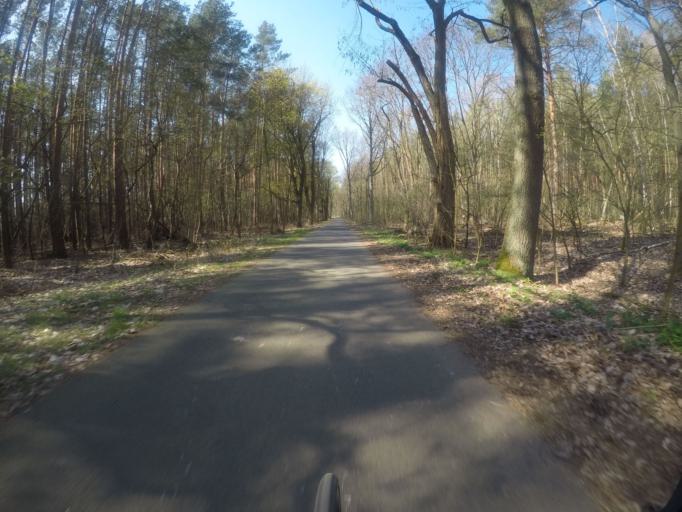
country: DE
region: Brandenburg
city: Brieselang
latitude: 52.6377
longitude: 13.0607
